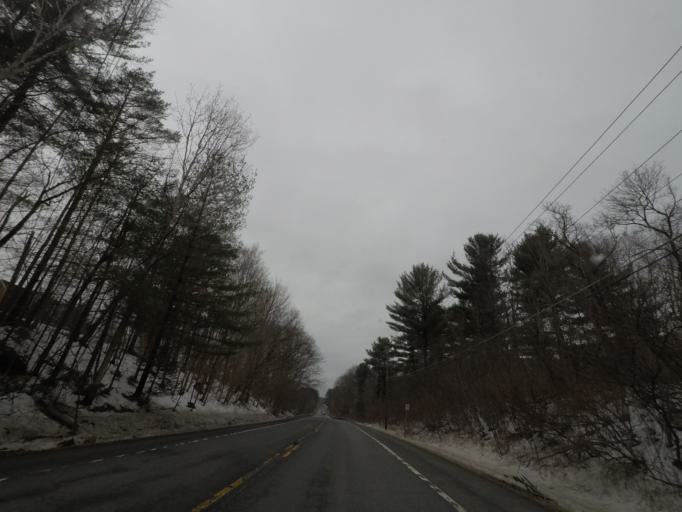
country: US
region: New York
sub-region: Schenectady County
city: Rotterdam
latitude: 42.7313
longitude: -73.9750
